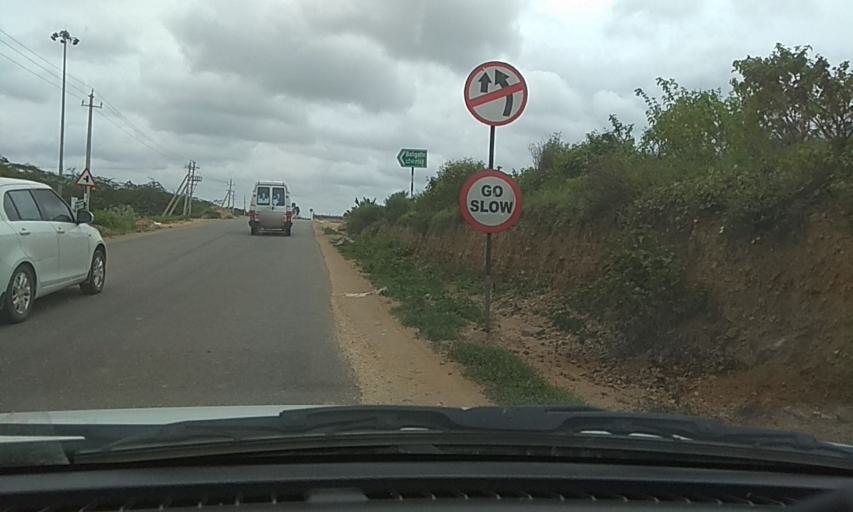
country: IN
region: Karnataka
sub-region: Chitradurga
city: Chitradurga
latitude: 14.2907
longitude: 76.2869
